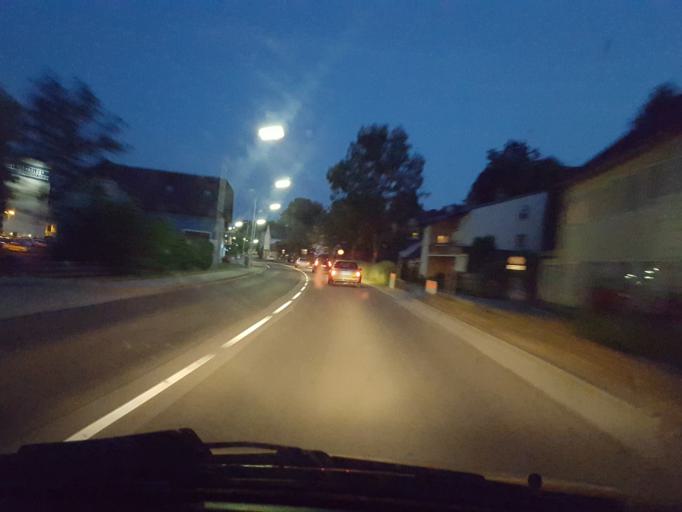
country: AT
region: Lower Austria
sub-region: Politischer Bezirk Scheibbs
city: Wieselburg
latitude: 48.1252
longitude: 15.1373
